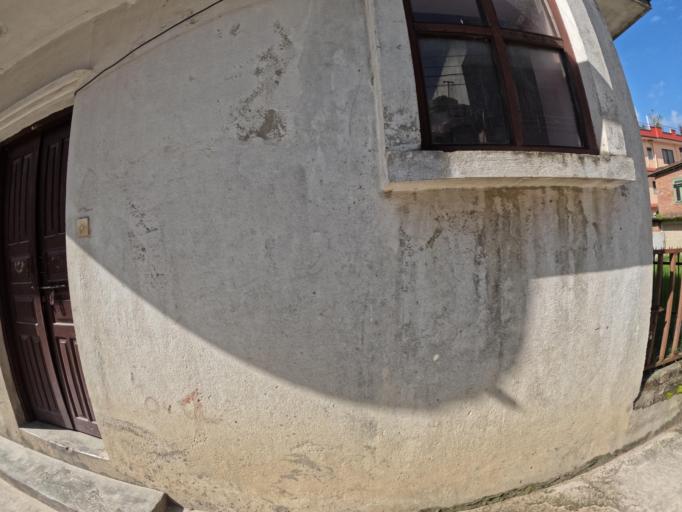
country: NP
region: Central Region
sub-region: Bagmati Zone
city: Kathmandu
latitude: 27.7566
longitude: 85.3337
